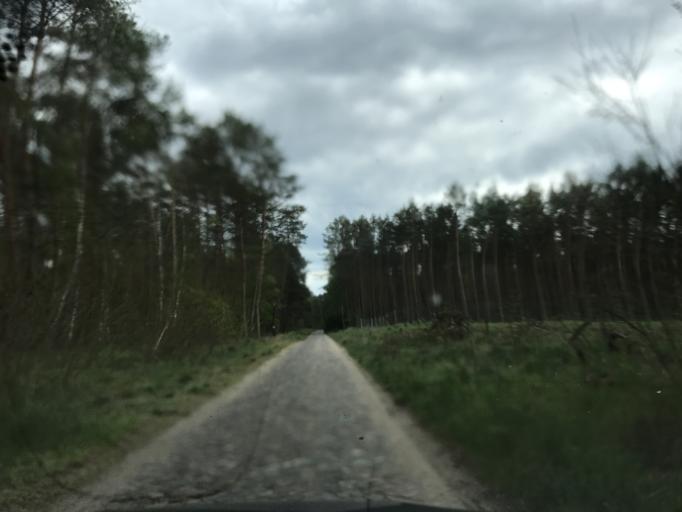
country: PL
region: West Pomeranian Voivodeship
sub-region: Powiat mysliborski
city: Mysliborz
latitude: 52.8733
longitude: 14.8719
